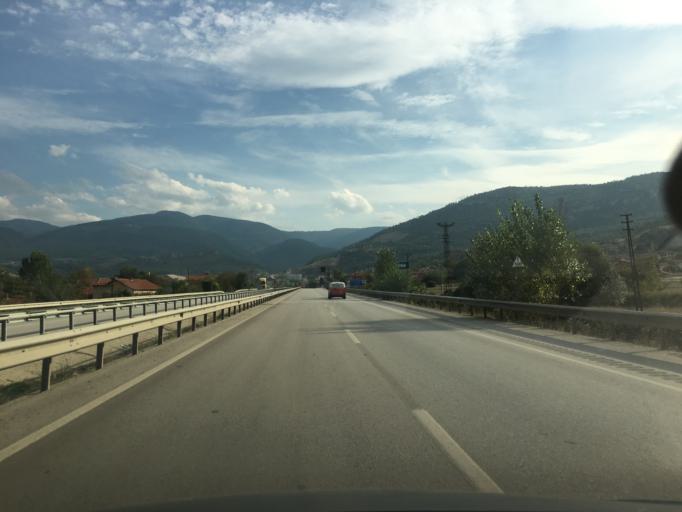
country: TR
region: Karabuk
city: Karabuk
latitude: 41.1074
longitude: 32.6687
